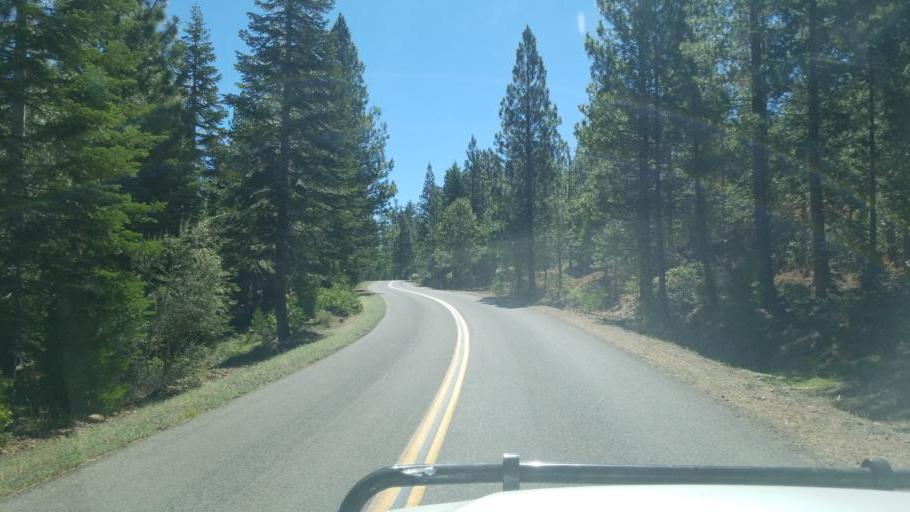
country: US
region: California
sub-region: Lassen County
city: Susanville
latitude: 40.5101
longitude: -120.7726
